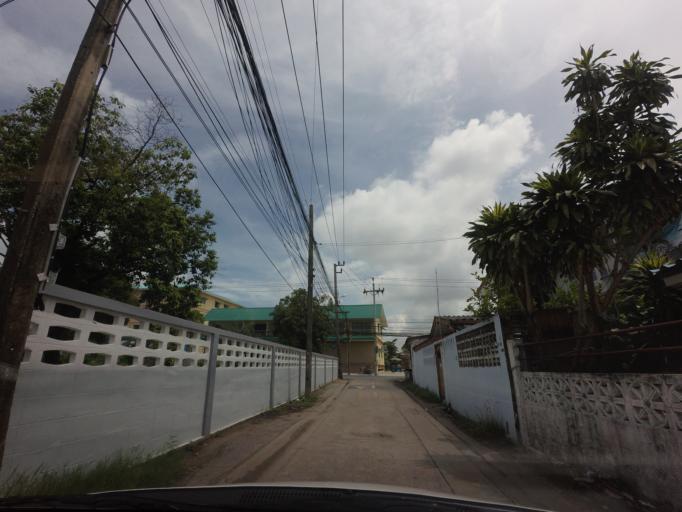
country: TH
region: Bangkok
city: Thung Khru
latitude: 13.6421
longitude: 100.5035
